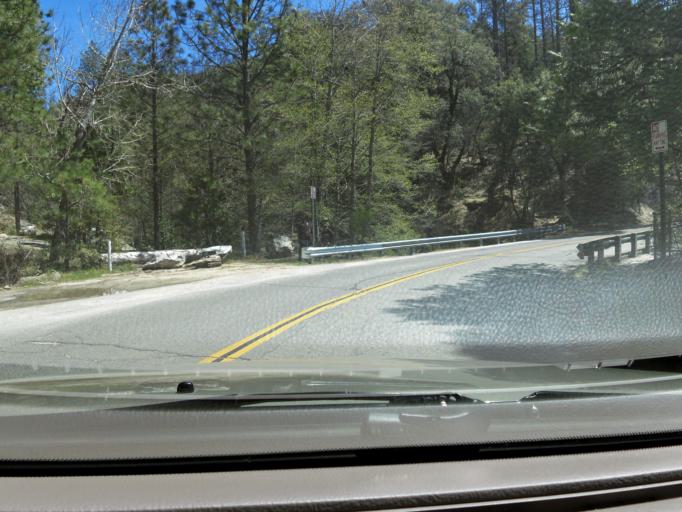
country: US
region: California
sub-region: Madera County
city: Oakhurst
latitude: 37.3323
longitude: -119.5719
